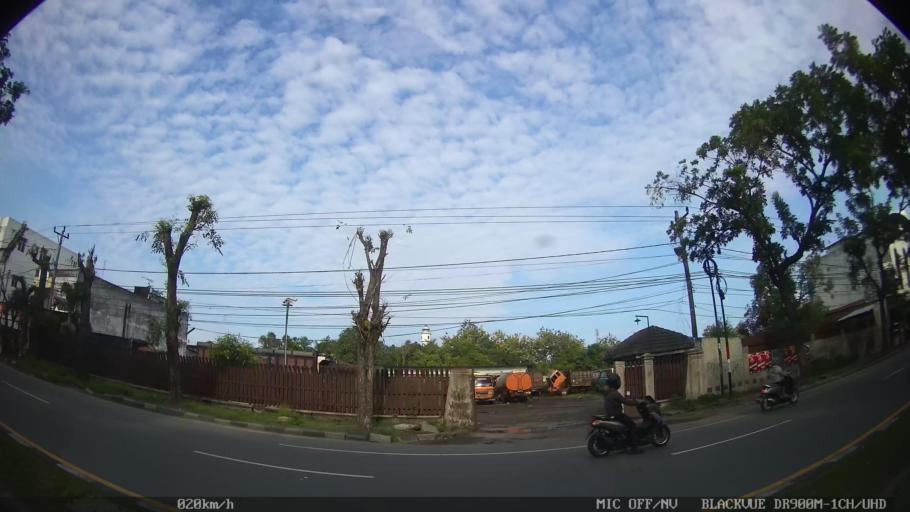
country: ID
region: North Sumatra
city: Medan
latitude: 3.6333
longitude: 98.6812
